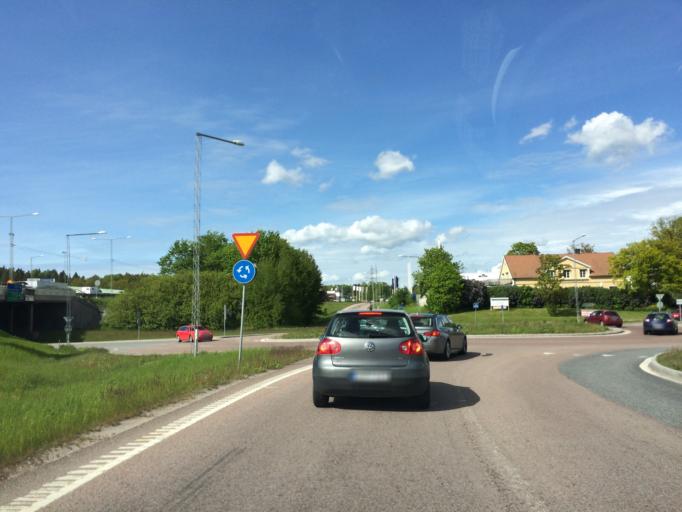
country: SE
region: Stockholm
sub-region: Danderyds Kommun
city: Djursholm
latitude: 59.4089
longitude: 18.0350
